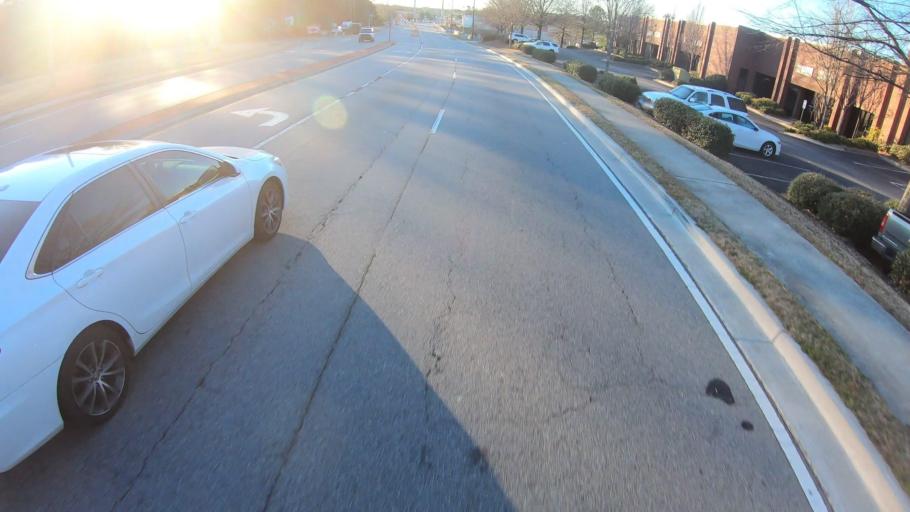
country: US
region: Georgia
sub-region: Cobb County
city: Kennesaw
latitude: 34.0463
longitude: -84.6072
